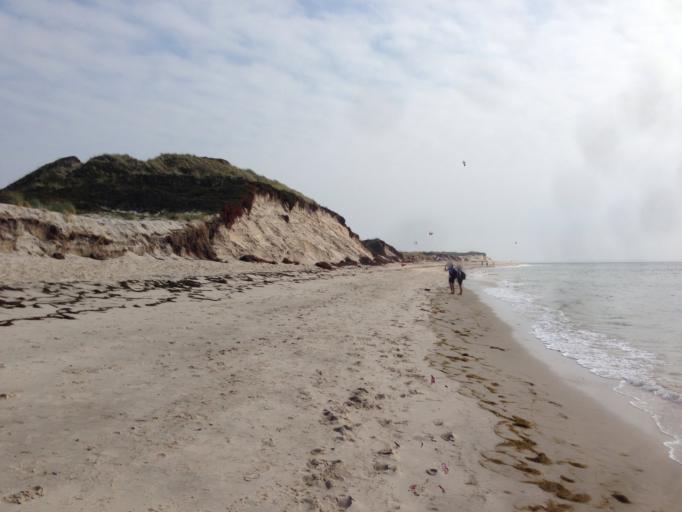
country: DE
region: Schleswig-Holstein
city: Norddorf
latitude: 54.7472
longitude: 8.2899
